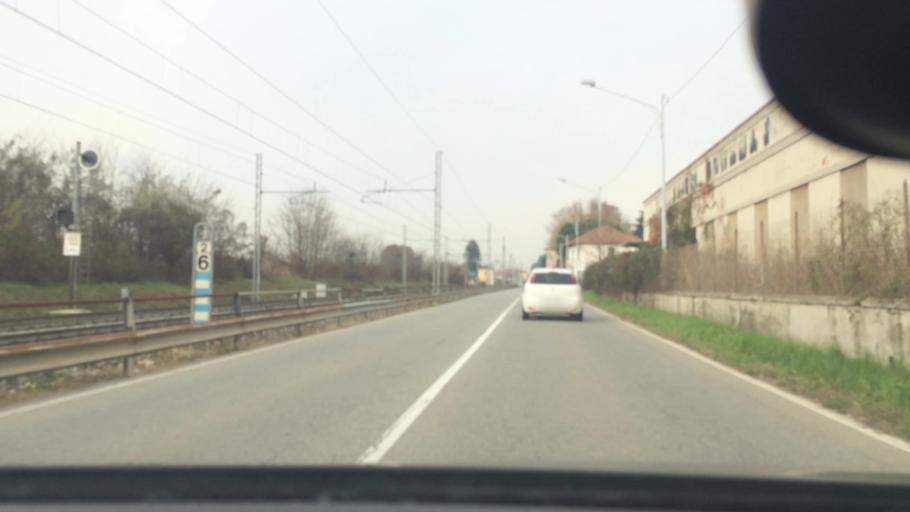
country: IT
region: Lombardy
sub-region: Provincia di Como
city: Rovello Porro
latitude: 45.6626
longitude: 9.0383
